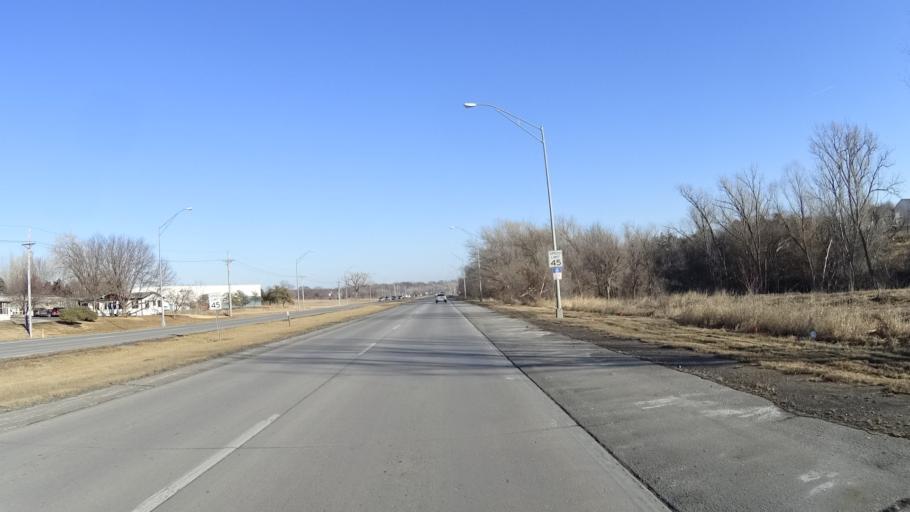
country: US
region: Nebraska
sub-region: Douglas County
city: Bennington
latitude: 41.2921
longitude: -96.1120
